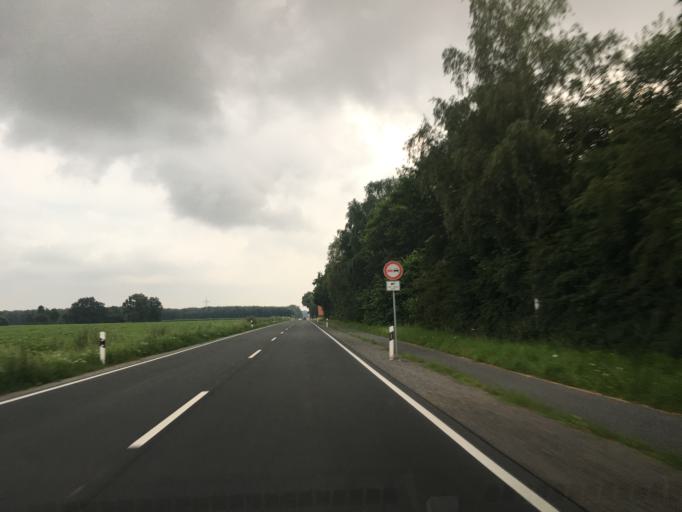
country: DE
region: North Rhine-Westphalia
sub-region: Regierungsbezirk Munster
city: Muenster
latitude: 52.0253
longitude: 7.6179
